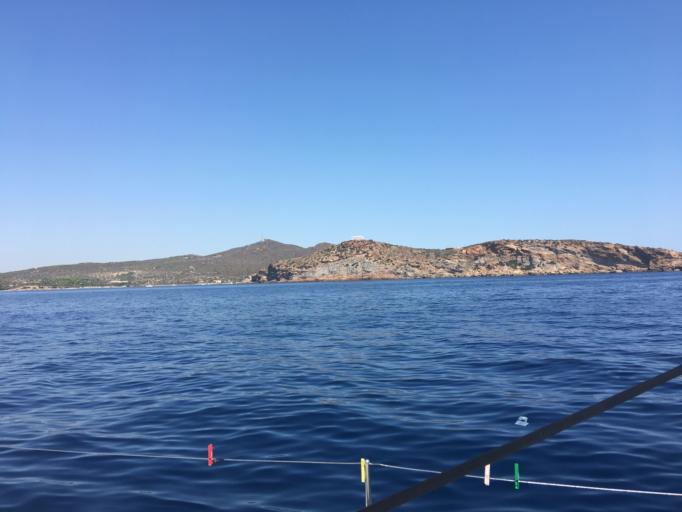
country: GR
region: Attica
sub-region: Nomarchia Anatolikis Attikis
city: Lavrio
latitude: 37.6406
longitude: 24.0238
